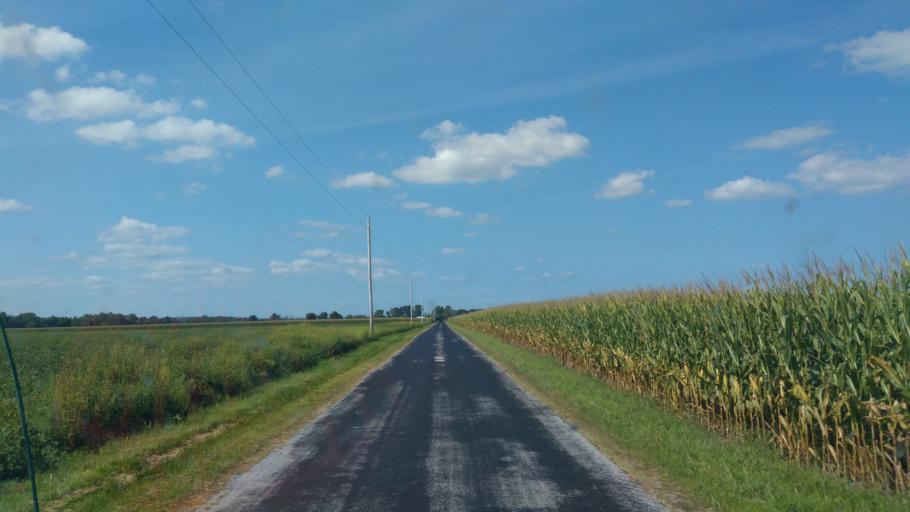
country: US
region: Ohio
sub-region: Hardin County
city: Forest
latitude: 40.7019
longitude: -83.4780
